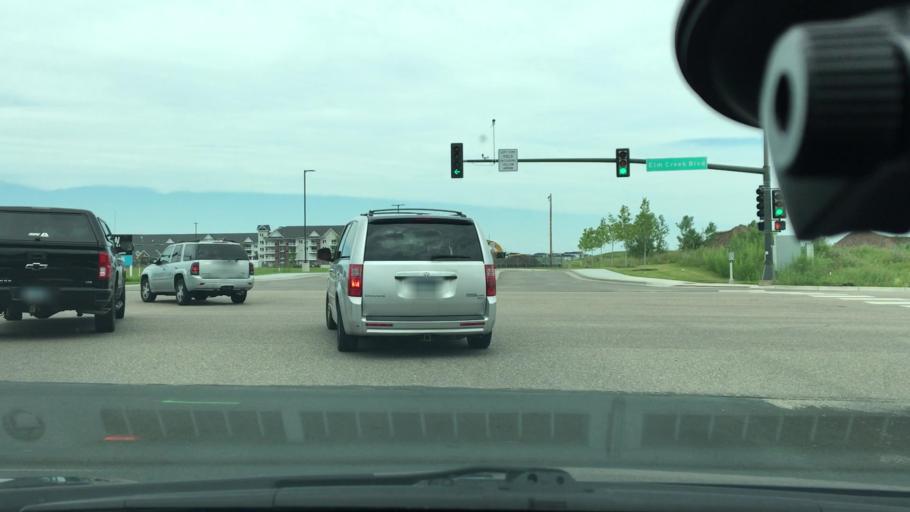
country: US
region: Minnesota
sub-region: Hennepin County
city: Osseo
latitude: 45.0945
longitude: -93.4269
